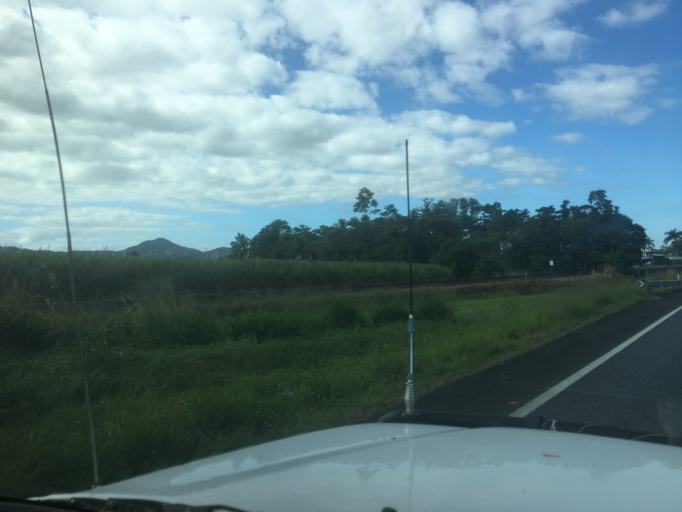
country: AU
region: Queensland
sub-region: Cassowary Coast
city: Innisfail
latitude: -17.2764
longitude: 145.9214
